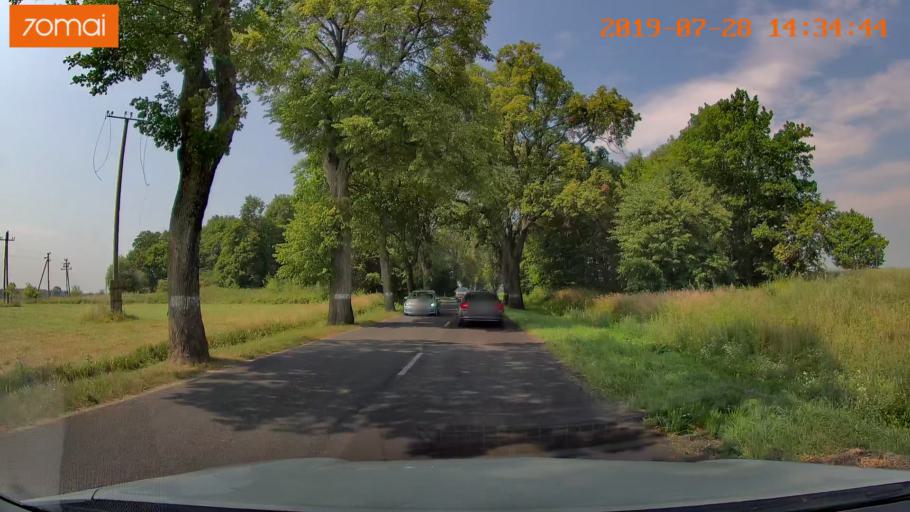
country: RU
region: Kaliningrad
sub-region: Gorod Kaliningrad
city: Yantarnyy
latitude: 54.8270
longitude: 20.0150
